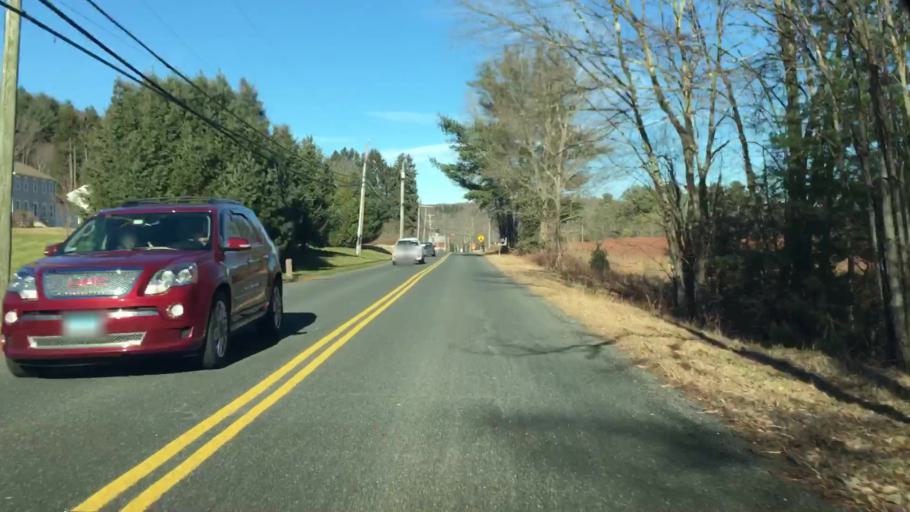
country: US
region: Connecticut
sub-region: Tolland County
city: Crystal Lake
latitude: 41.9257
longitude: -72.3888
